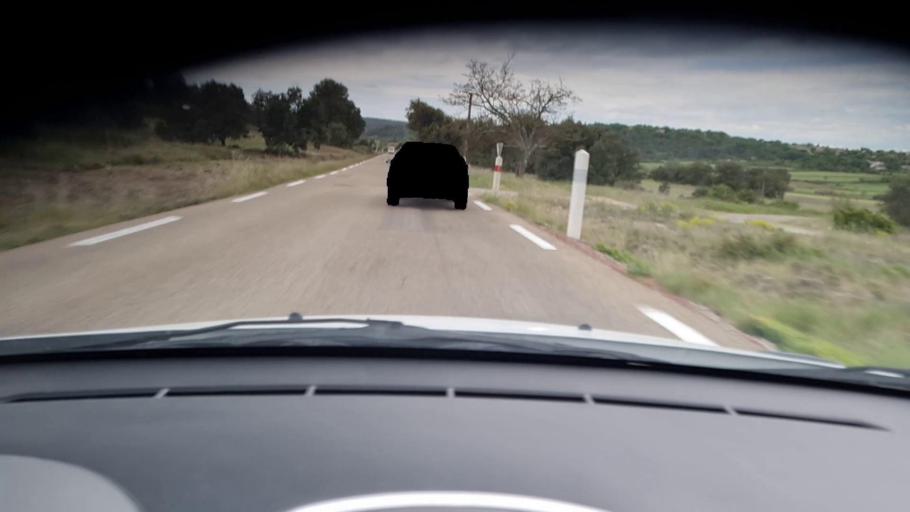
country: FR
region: Languedoc-Roussillon
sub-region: Departement du Gard
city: Blauzac
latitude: 43.9663
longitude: 4.3870
